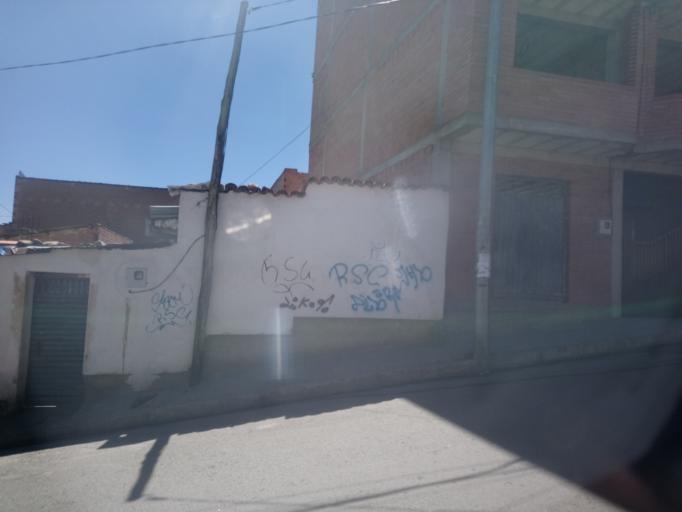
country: BO
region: La Paz
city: La Paz
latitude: -16.4893
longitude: -68.1044
